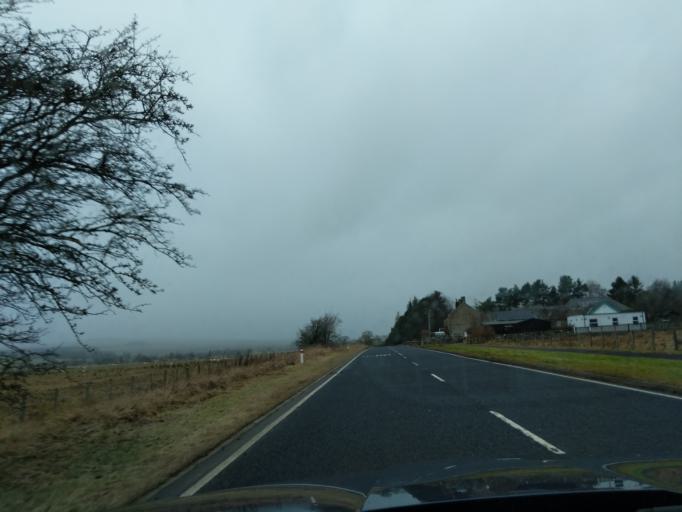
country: GB
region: England
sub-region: Northumberland
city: Otterburn
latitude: 55.2369
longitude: -2.1974
